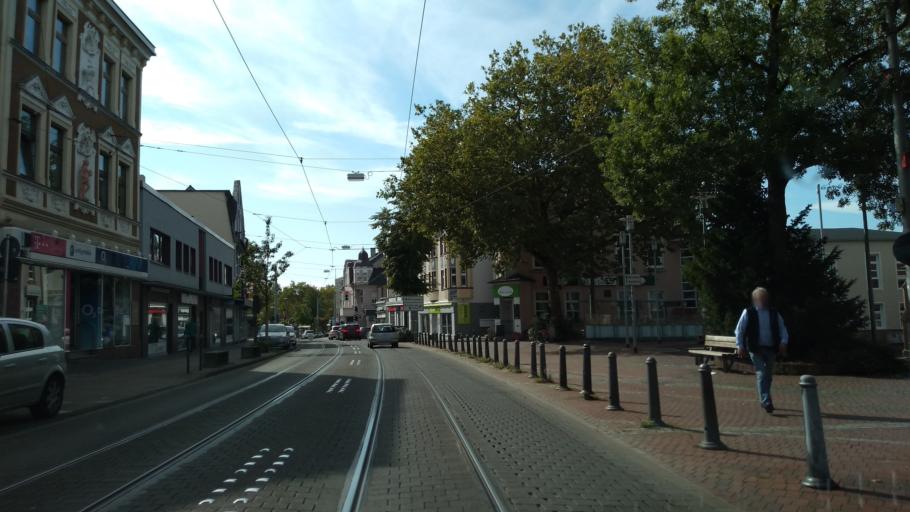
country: DE
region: North Rhine-Westphalia
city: Hattingen
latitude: 51.4271
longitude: 7.1621
